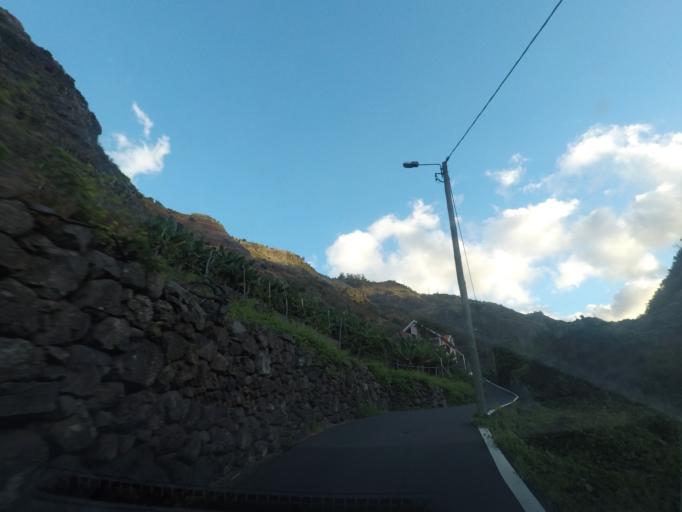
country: PT
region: Madeira
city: Ponta do Sol
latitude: 32.6864
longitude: -17.0754
